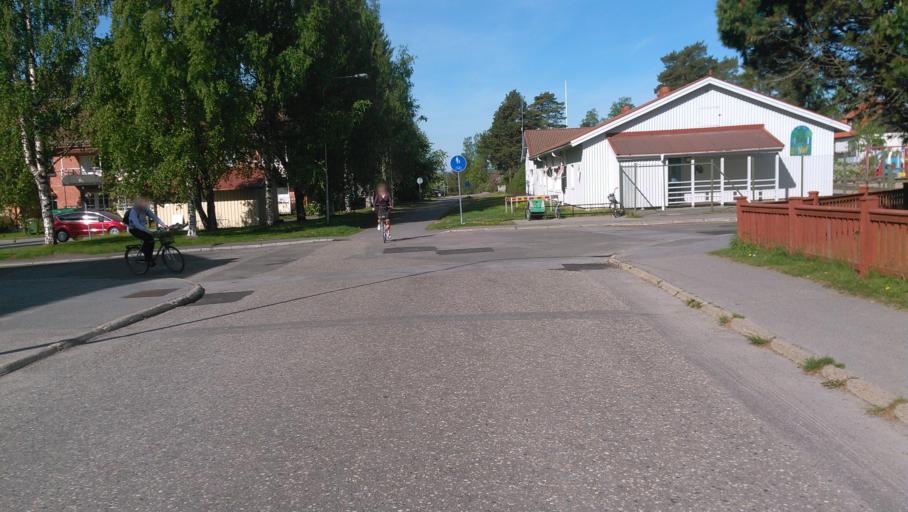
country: SE
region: Vaesterbotten
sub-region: Umea Kommun
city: Umea
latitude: 63.8100
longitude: 20.3035
